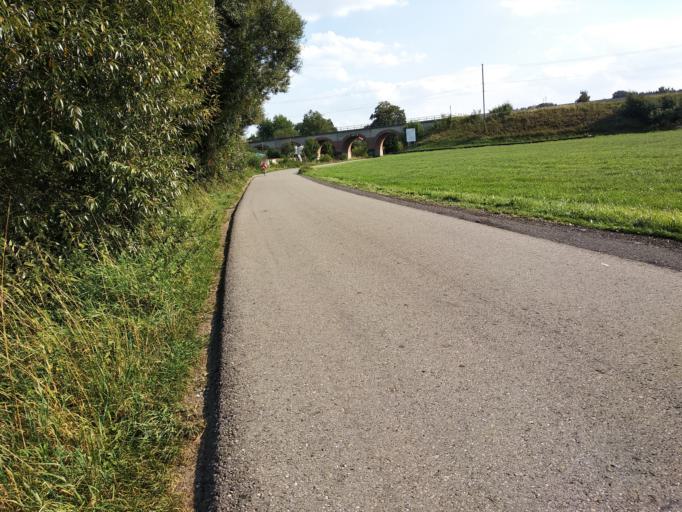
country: DE
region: Bavaria
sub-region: Swabia
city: Westerheim
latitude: 48.0177
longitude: 10.2978
